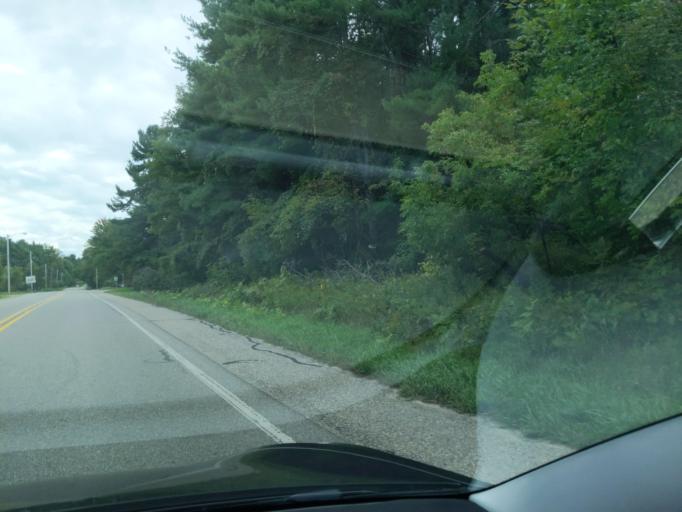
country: US
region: Michigan
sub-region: Kalkaska County
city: Rapid City
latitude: 44.8894
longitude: -85.2723
